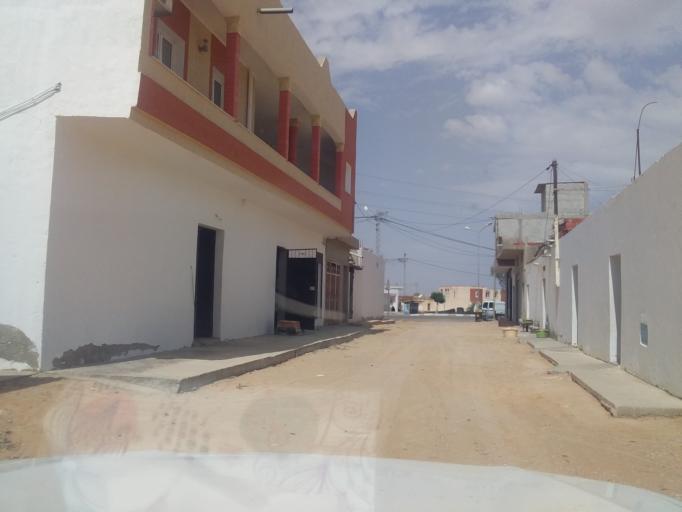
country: TN
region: Madanin
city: Medenine
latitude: 33.5832
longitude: 10.3188
